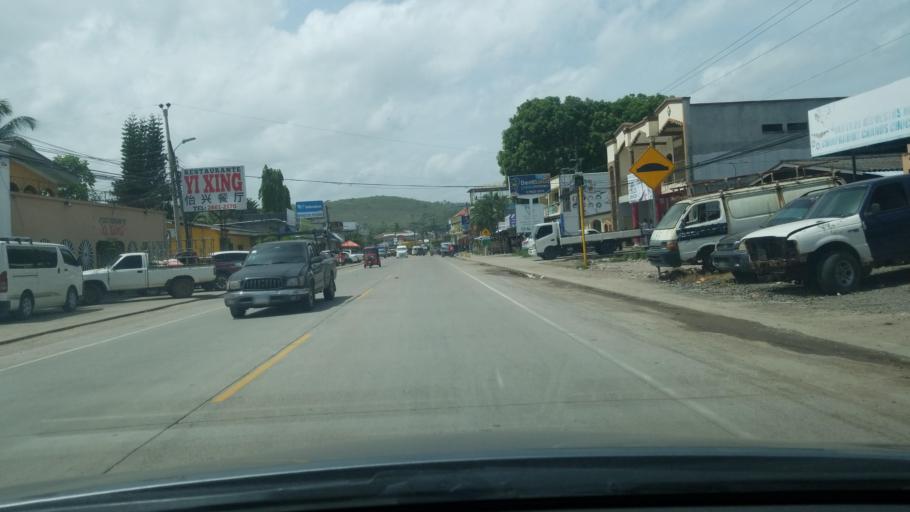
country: HN
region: Copan
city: La Entrada
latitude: 15.0638
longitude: -88.7574
